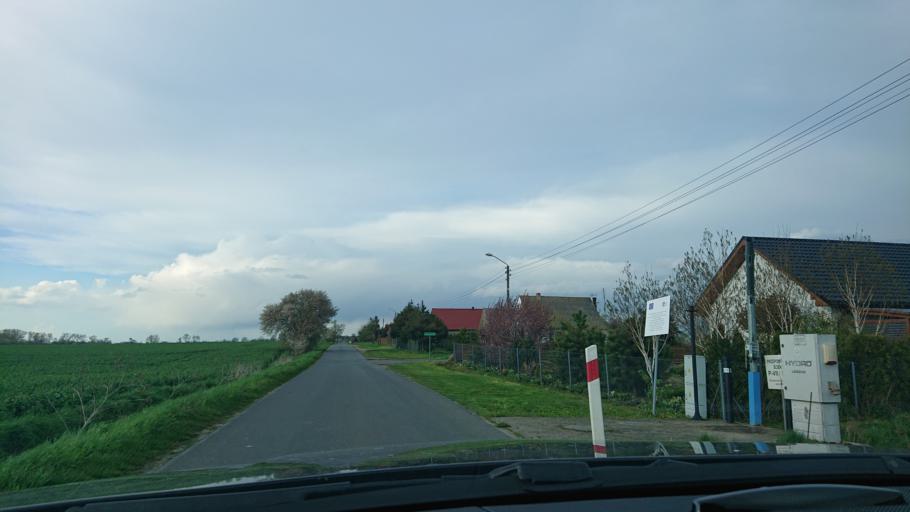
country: PL
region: Greater Poland Voivodeship
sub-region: Powiat gnieznienski
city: Klecko
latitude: 52.5793
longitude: 17.4803
